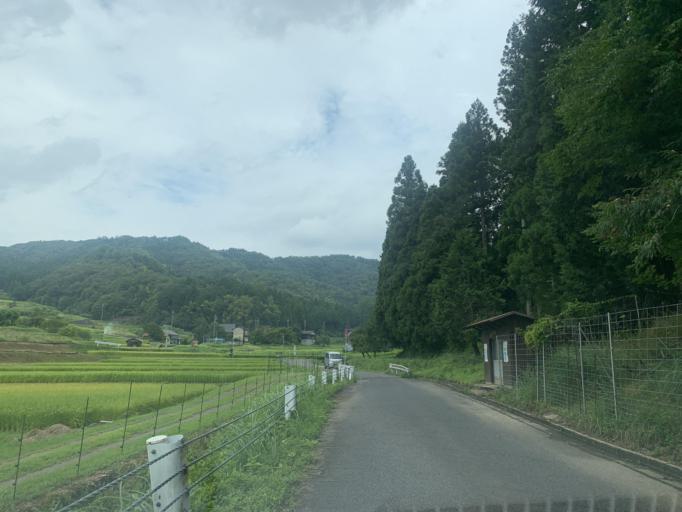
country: JP
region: Kyoto
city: Miyazu
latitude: 35.4441
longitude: 135.1609
